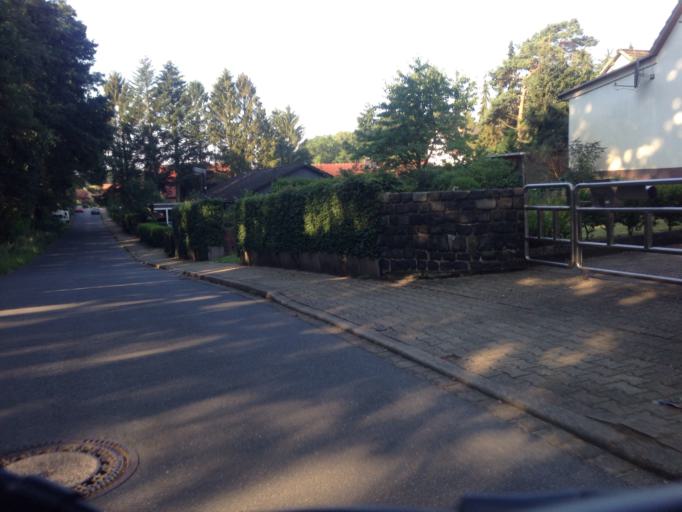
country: DE
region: Lower Saxony
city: Adendorf
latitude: 53.2748
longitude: 10.4445
